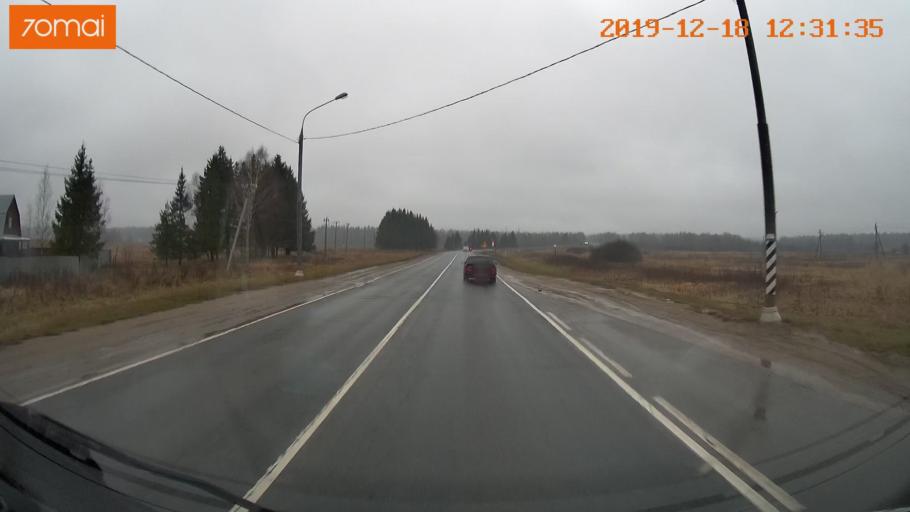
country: RU
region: Moskovskaya
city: Rumyantsevo
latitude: 56.1005
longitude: 36.5431
